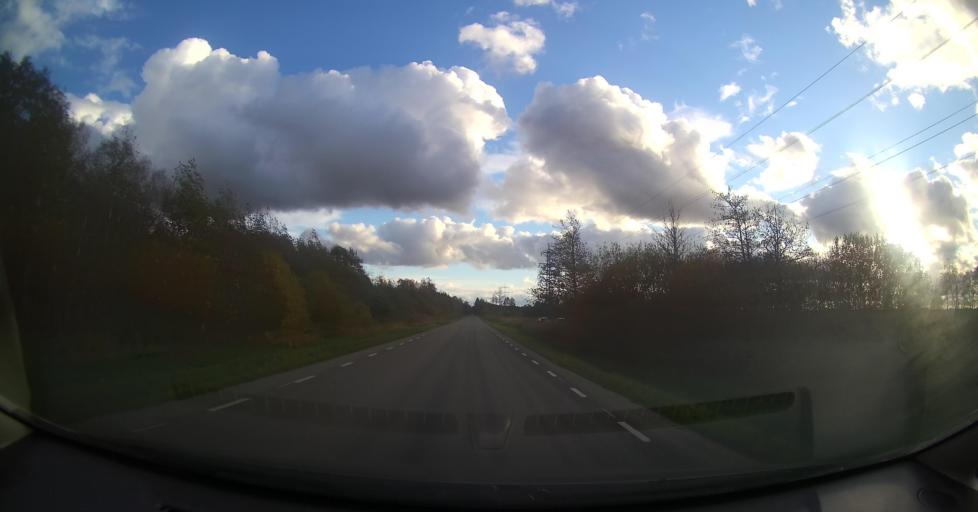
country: EE
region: Harju
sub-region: Maardu linn
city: Maardu
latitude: 59.4446
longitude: 25.0145
